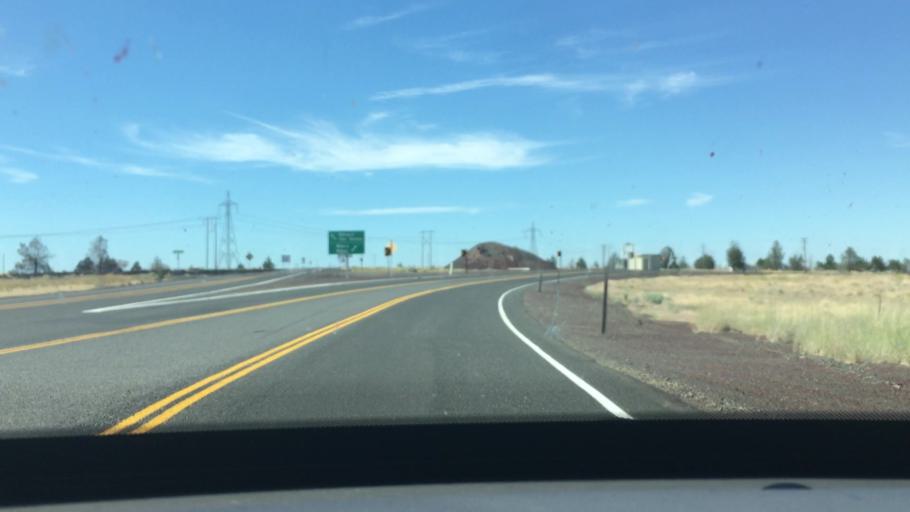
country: US
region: Oregon
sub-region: Jefferson County
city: Madras
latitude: 44.9197
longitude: -120.9453
